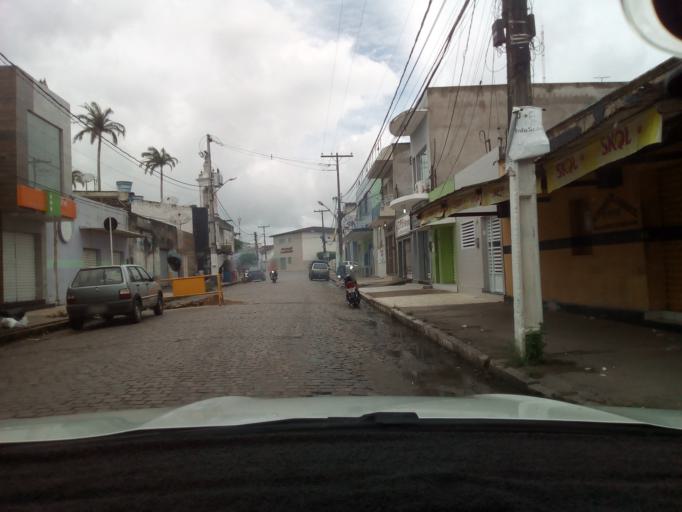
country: BR
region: Paraiba
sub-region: Pedras De Fogo
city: Pedras de Fogo
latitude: -7.4047
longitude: -35.1179
